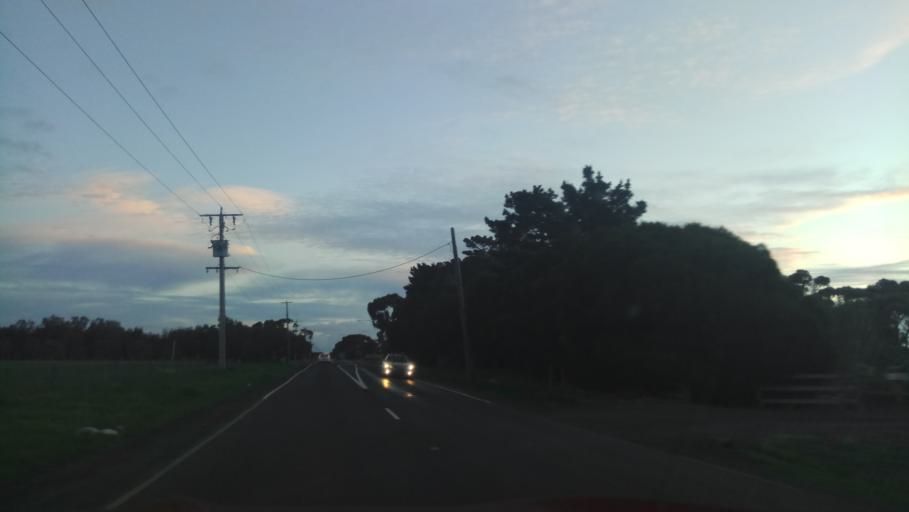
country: AU
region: Victoria
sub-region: Wyndham
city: Point Cook
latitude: -37.9159
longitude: 144.7508
